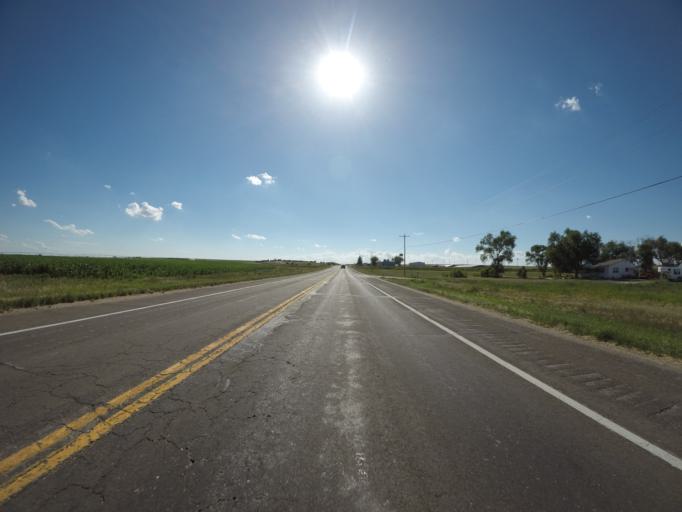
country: US
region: Colorado
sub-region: Logan County
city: Sterling
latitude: 40.6239
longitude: -103.3061
